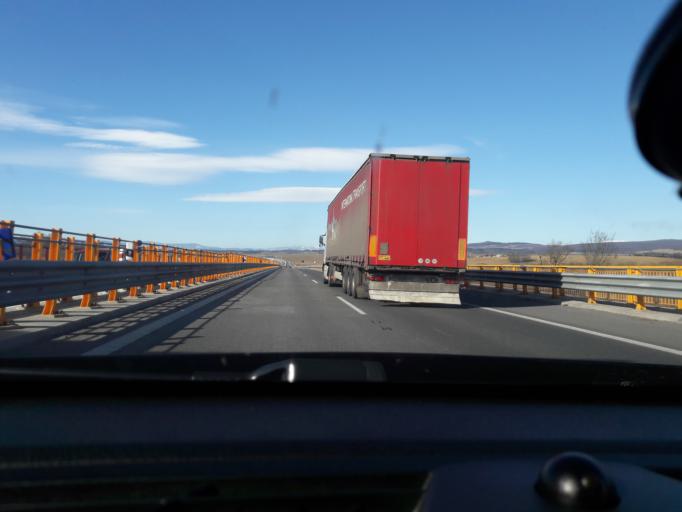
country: SK
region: Banskobystricky
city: Detva
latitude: 48.5501
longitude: 19.3249
